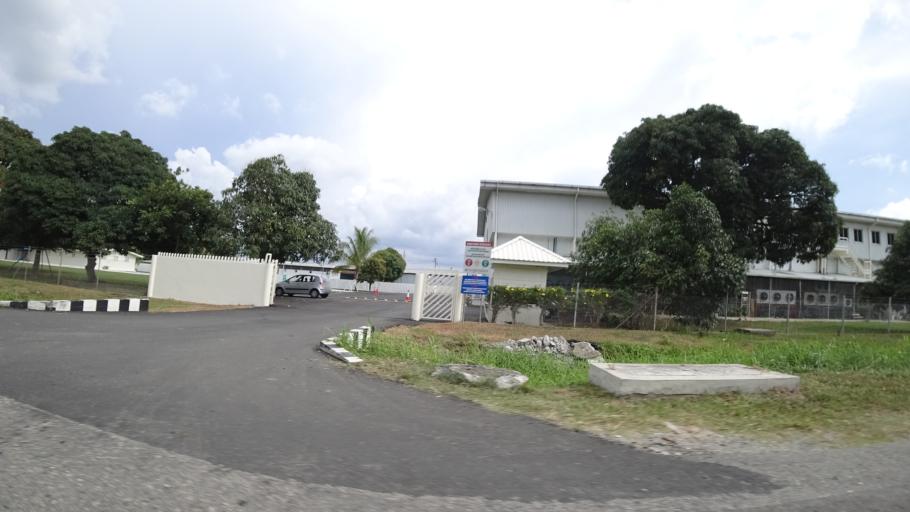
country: BN
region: Brunei and Muara
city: Bandar Seri Begawan
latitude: 4.8249
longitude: 114.8548
